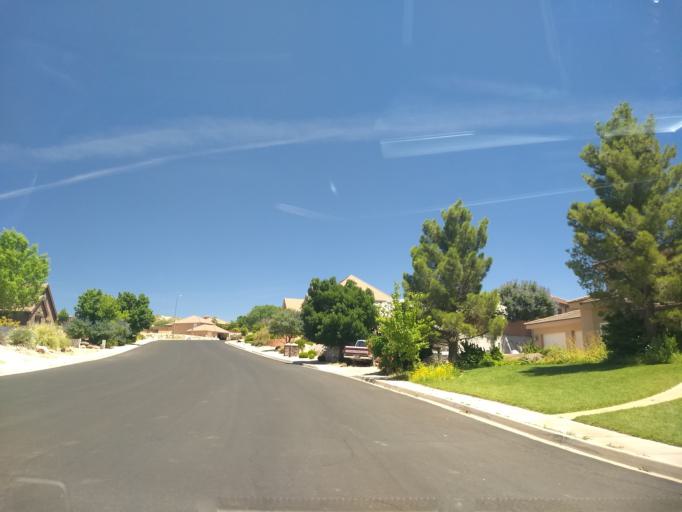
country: US
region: Utah
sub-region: Washington County
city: Washington
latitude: 37.0887
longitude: -113.4897
